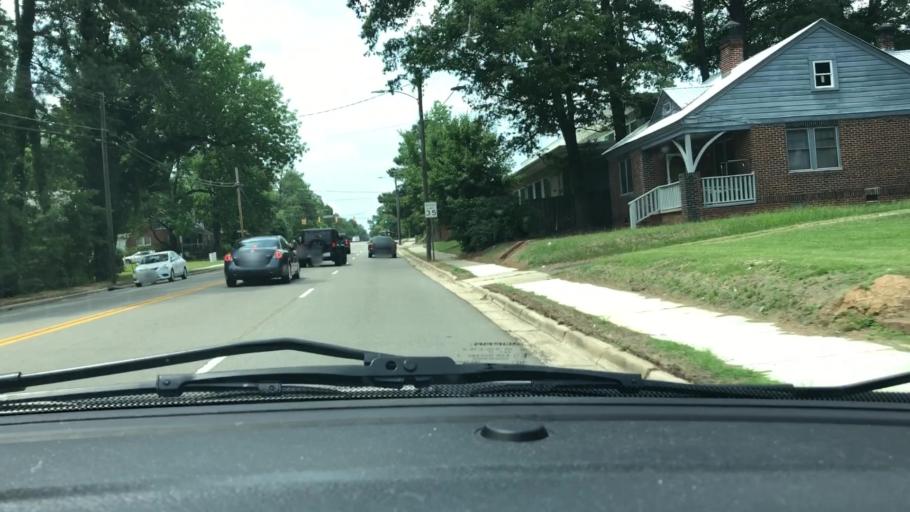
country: US
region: North Carolina
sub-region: Lee County
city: Sanford
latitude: 35.4841
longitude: -79.1840
